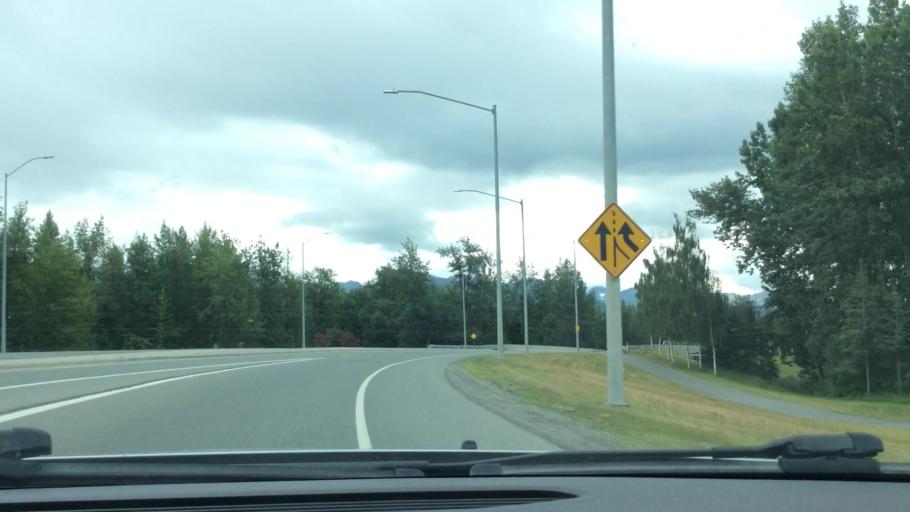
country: US
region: Alaska
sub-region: Anchorage Municipality
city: Anchorage
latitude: 61.2402
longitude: -149.7796
